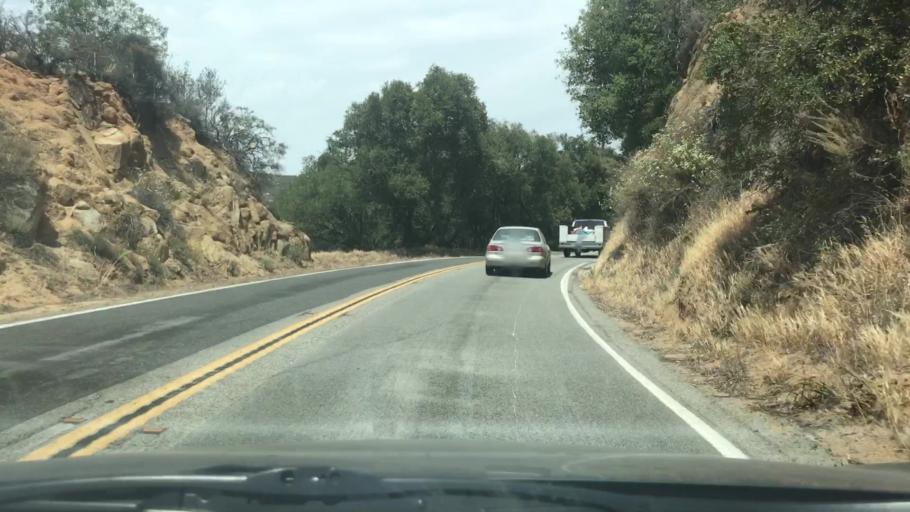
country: US
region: California
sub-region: Riverside County
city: Lakeland Village
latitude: 33.6054
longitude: -117.4473
